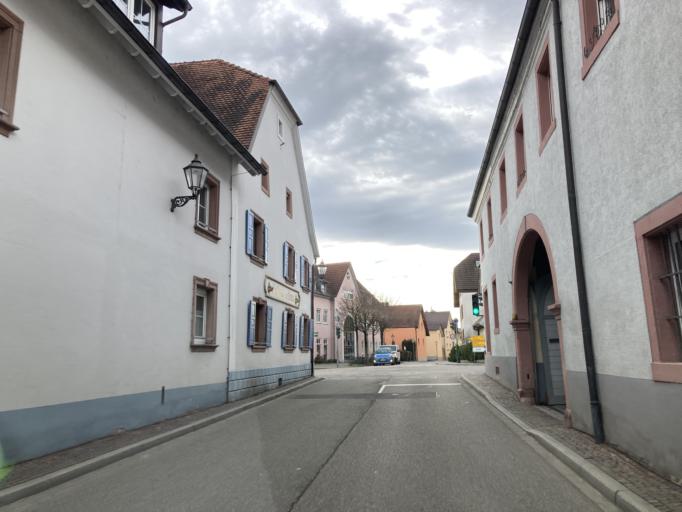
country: DE
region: Baden-Wuerttemberg
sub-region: Freiburg Region
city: Botzingen
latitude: 48.0717
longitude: 7.7189
